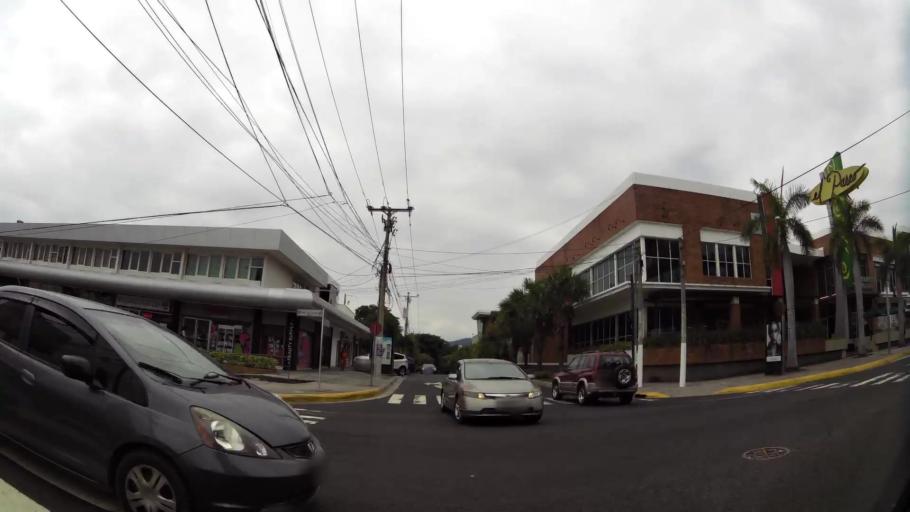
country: SV
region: La Libertad
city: Antiguo Cuscatlan
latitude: 13.7020
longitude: -89.2345
